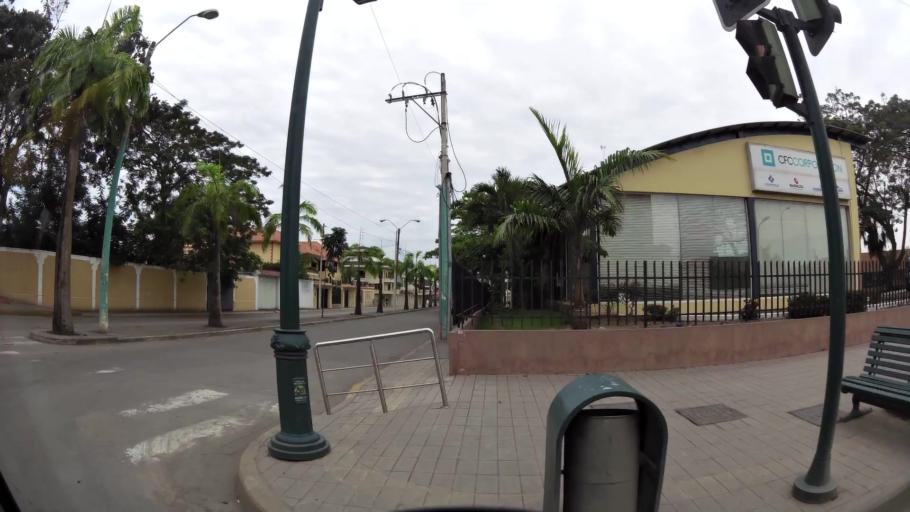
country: EC
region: El Oro
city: Machala
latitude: -3.2627
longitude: -79.9430
